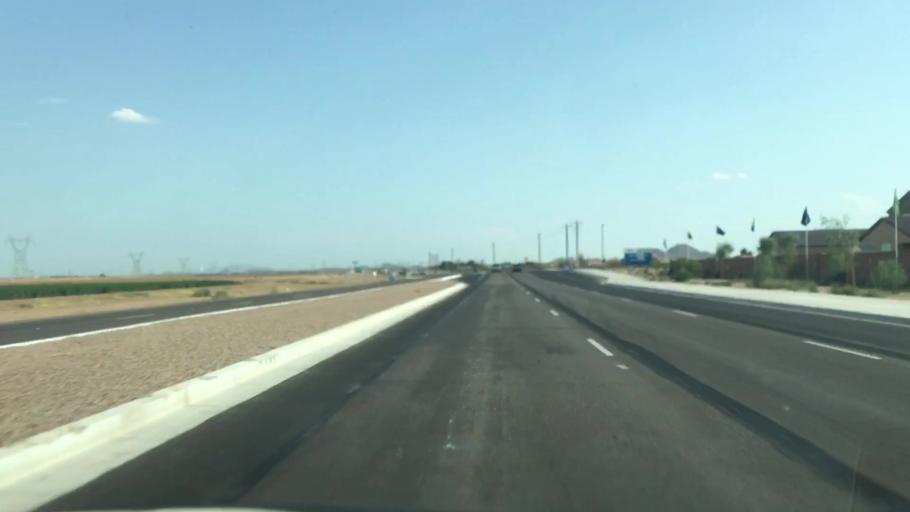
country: US
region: Arizona
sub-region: Pinal County
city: San Tan Valley
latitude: 33.2070
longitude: -111.5656
